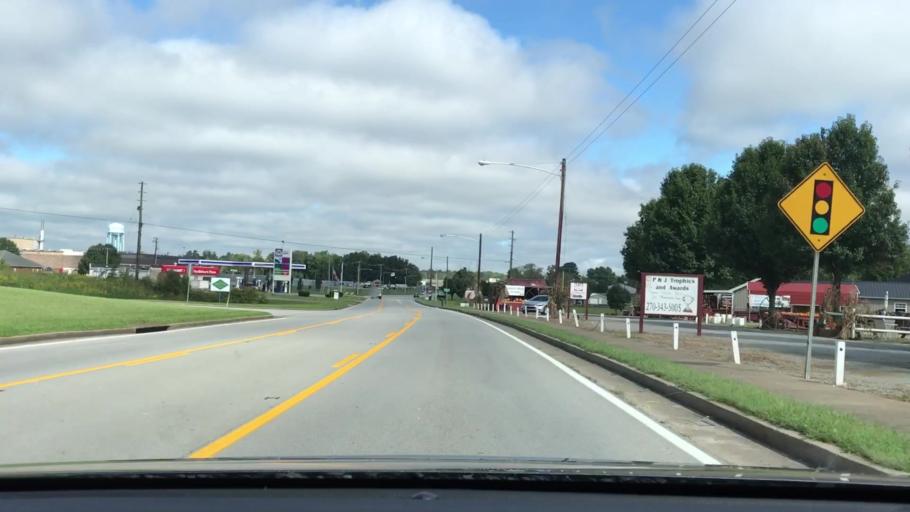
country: US
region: Kentucky
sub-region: Russell County
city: Jamestown
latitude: 37.0082
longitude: -85.0746
